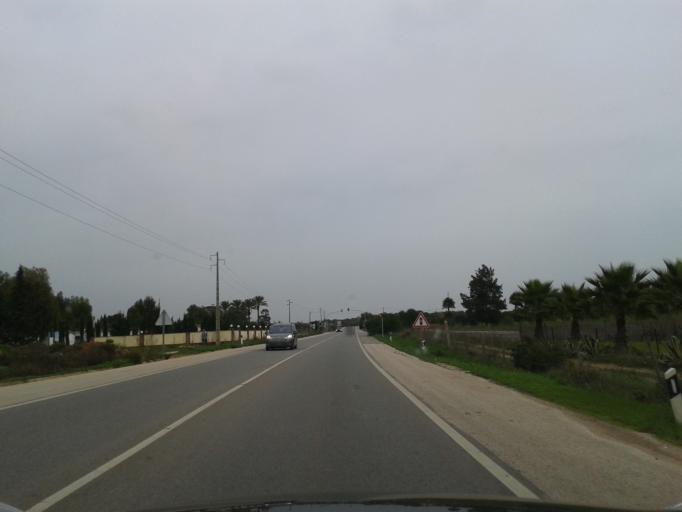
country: PT
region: Faro
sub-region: Lagos
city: Lagos
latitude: 37.1003
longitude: -8.7347
